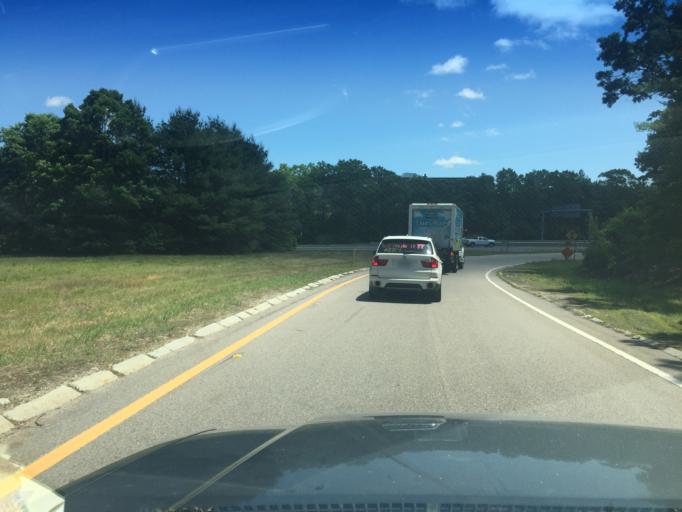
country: US
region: Massachusetts
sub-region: Bristol County
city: Mansfield
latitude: 42.0409
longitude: -71.2416
